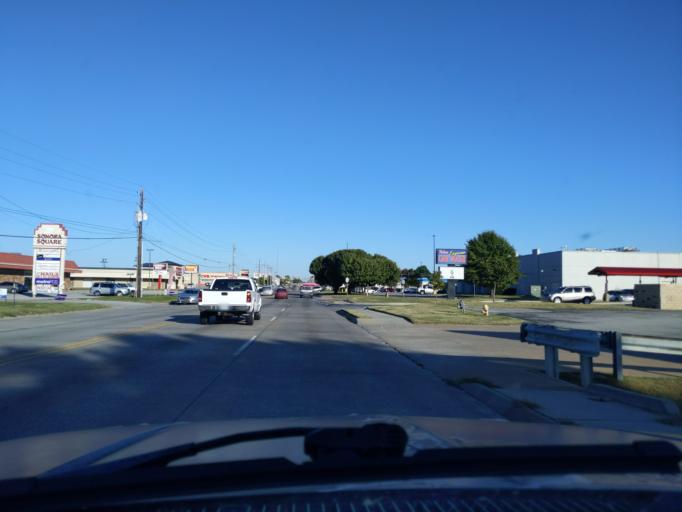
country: US
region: Oklahoma
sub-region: Tulsa County
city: Broken Arrow
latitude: 36.1189
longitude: -95.8549
